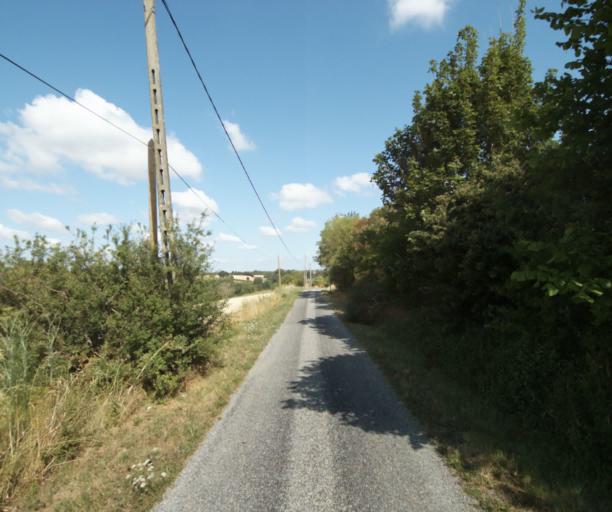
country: FR
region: Midi-Pyrenees
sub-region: Departement de la Haute-Garonne
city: Avignonet-Lauragais
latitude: 43.4360
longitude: 1.7908
